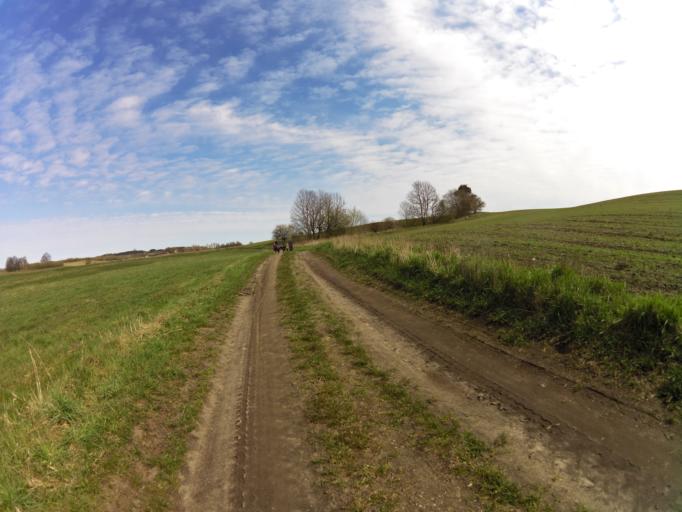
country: PL
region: West Pomeranian Voivodeship
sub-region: Powiat szczecinecki
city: Szczecinek
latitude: 53.7417
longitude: 16.5968
